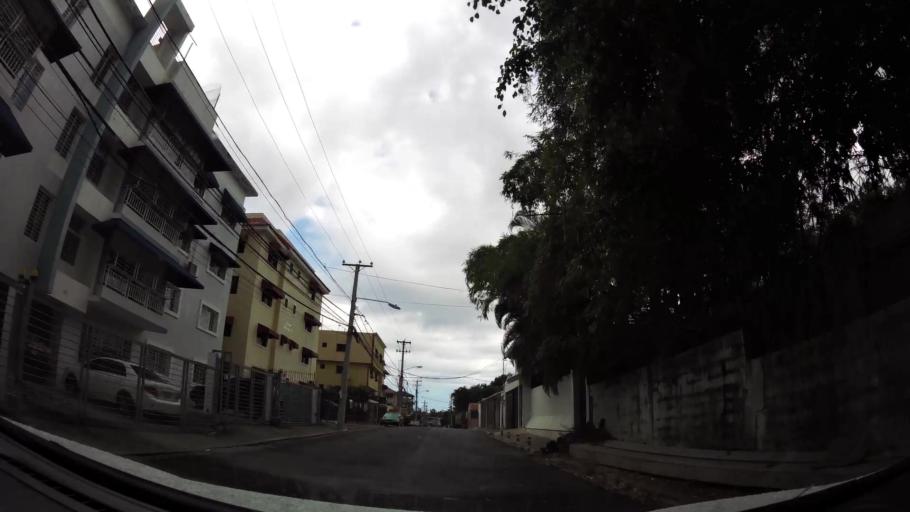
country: DO
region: Nacional
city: La Agustina
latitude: 18.5003
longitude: -69.9360
